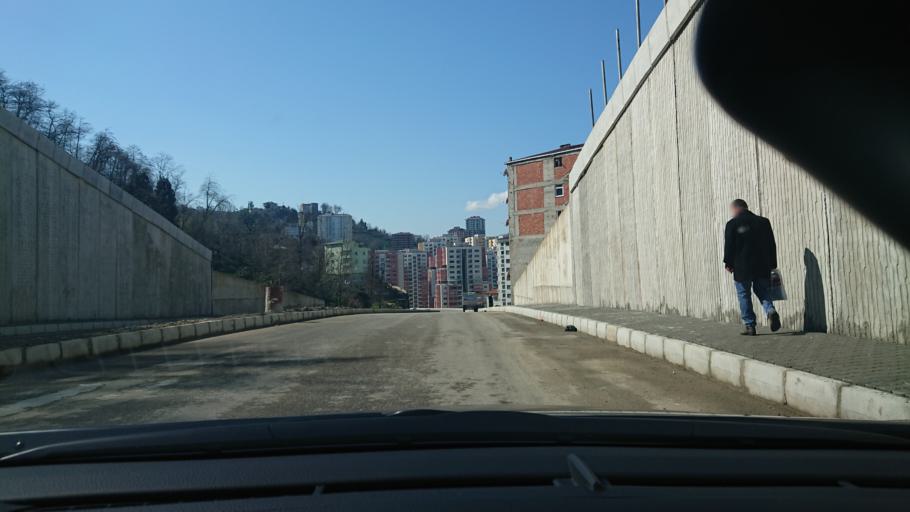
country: TR
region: Rize
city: Rize
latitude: 41.0183
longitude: 40.5198
